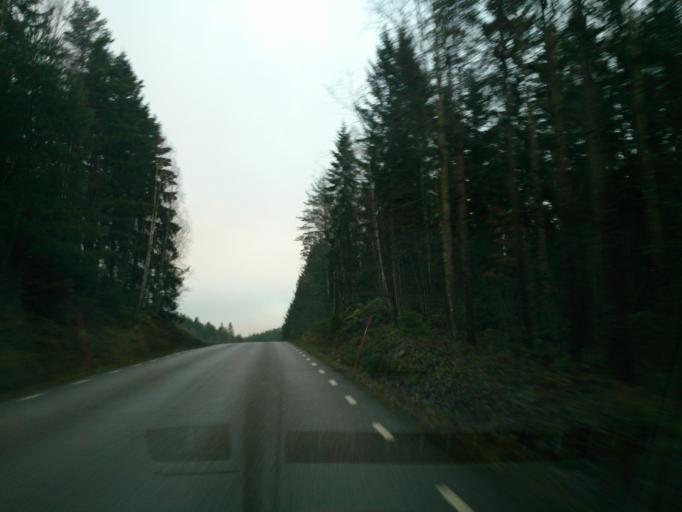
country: SE
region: OEstergoetland
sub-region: Atvidabergs Kommun
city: Atvidaberg
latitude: 58.3024
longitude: 16.0158
